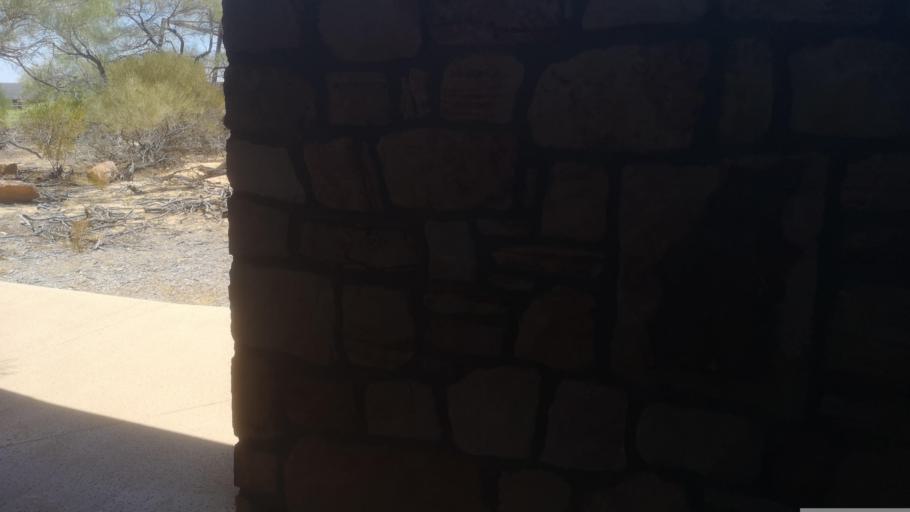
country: AU
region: Western Australia
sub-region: Northampton Shire
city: Kalbarri
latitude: -27.5546
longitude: 114.4334
